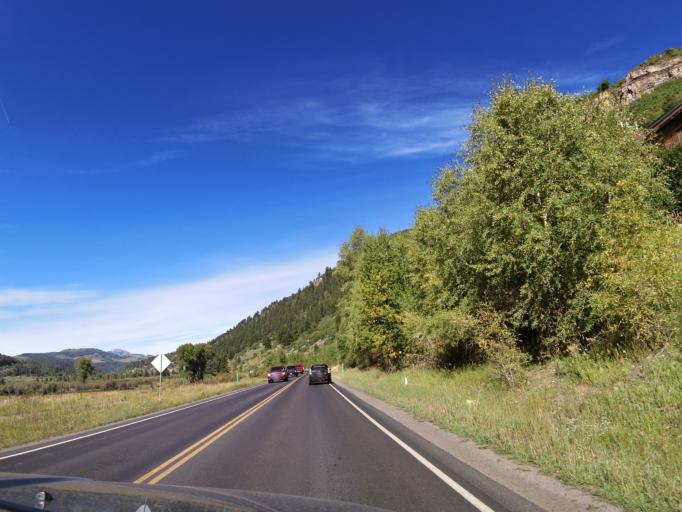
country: US
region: Colorado
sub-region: San Miguel County
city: Mountain Village
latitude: 37.9509
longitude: -107.8553
